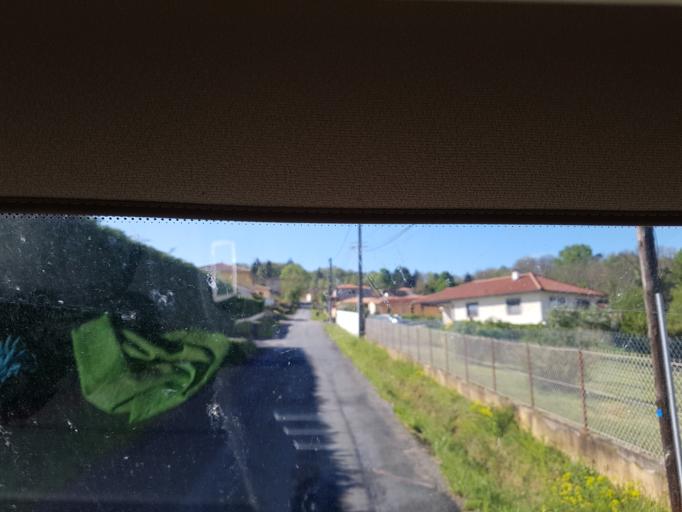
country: FR
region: Rhone-Alpes
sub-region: Departement du Rhone
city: Lentilly
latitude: 45.8074
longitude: 4.6532
